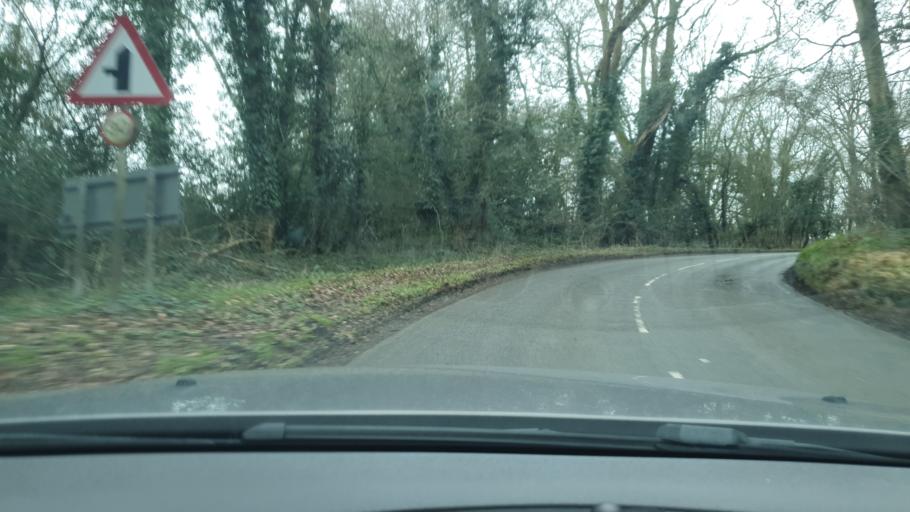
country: GB
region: England
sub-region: Oxfordshire
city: Rotherfield Peppard
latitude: 51.5399
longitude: -0.9562
